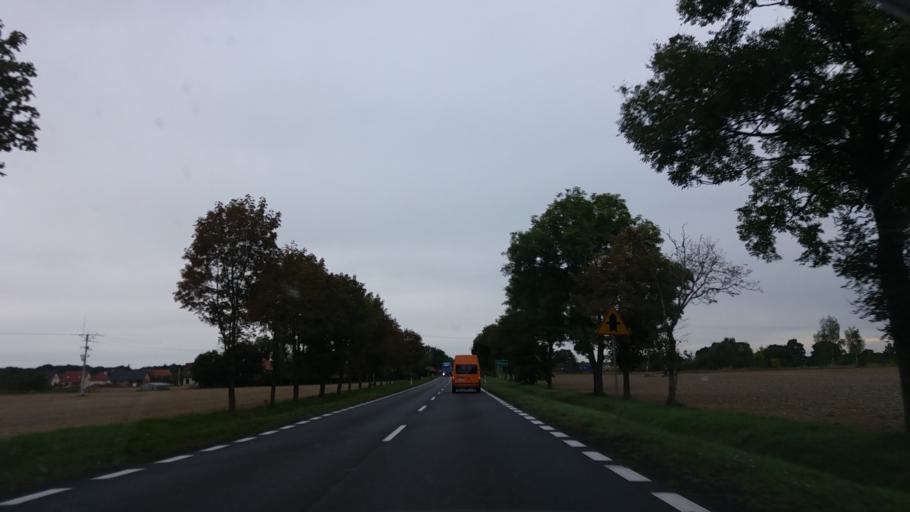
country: PL
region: Lower Silesian Voivodeship
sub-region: Powiat legnicki
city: Prochowice
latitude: 51.3294
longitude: 16.3074
